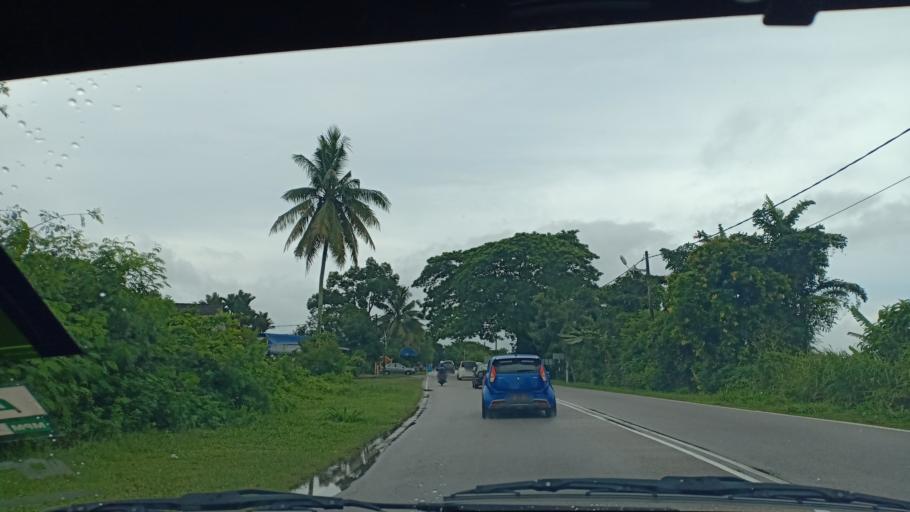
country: MY
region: Penang
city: Kepala Batas
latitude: 5.4926
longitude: 100.4563
